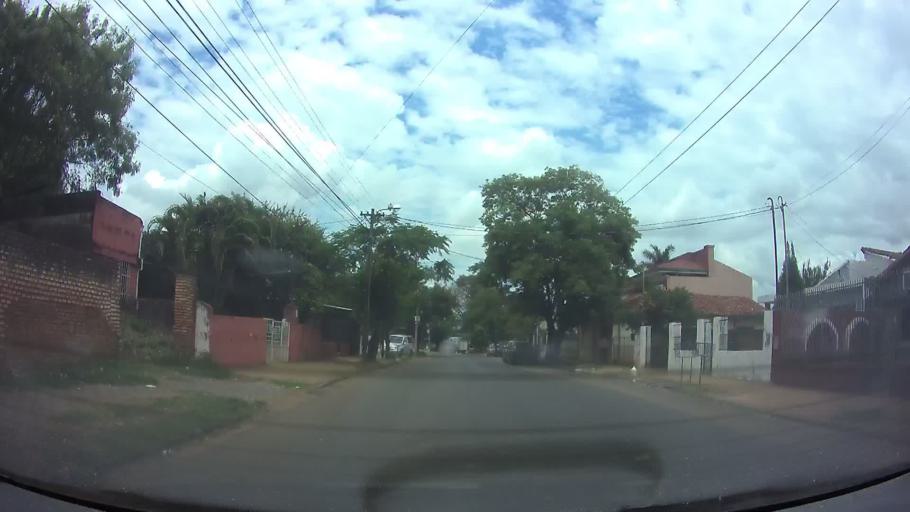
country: PY
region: Central
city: Lambare
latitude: -25.3255
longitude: -57.5841
